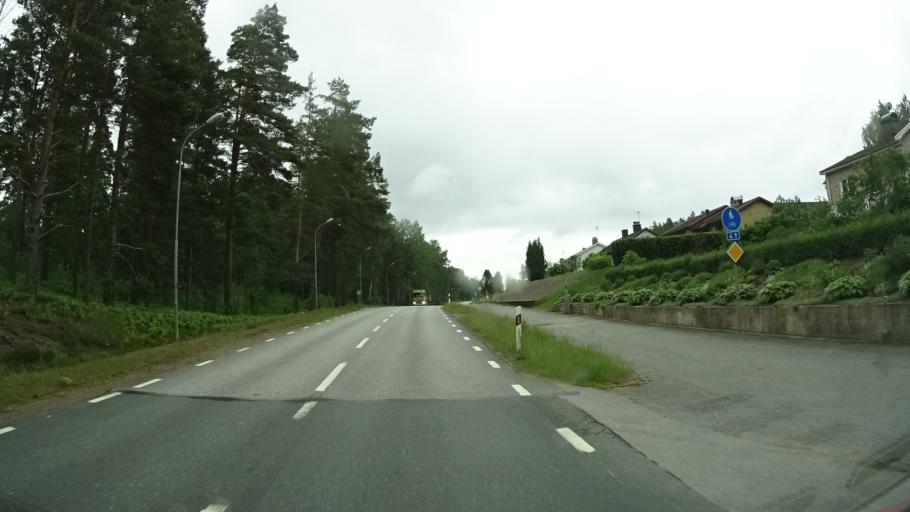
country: SE
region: Kalmar
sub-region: Hultsfreds Kommun
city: Hultsfred
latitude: 57.5456
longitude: 15.7373
